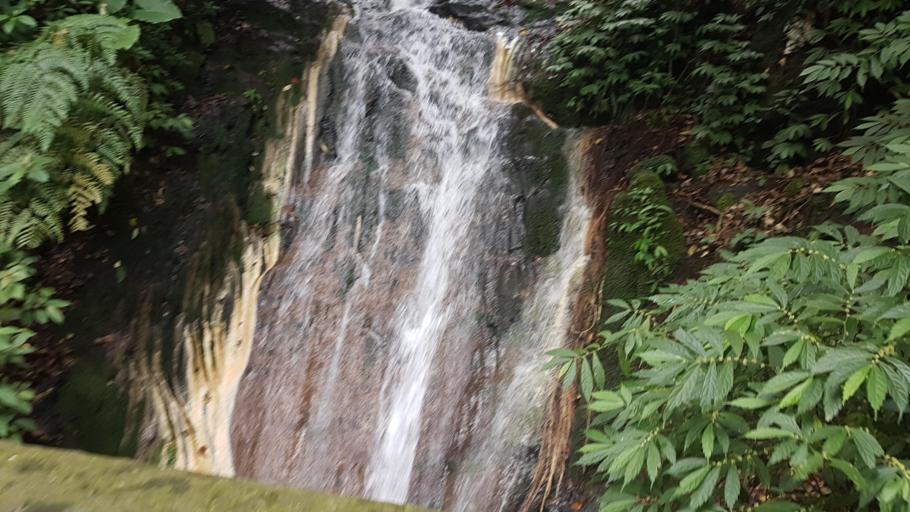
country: TW
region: Taipei
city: Taipei
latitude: 25.1570
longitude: 121.5412
